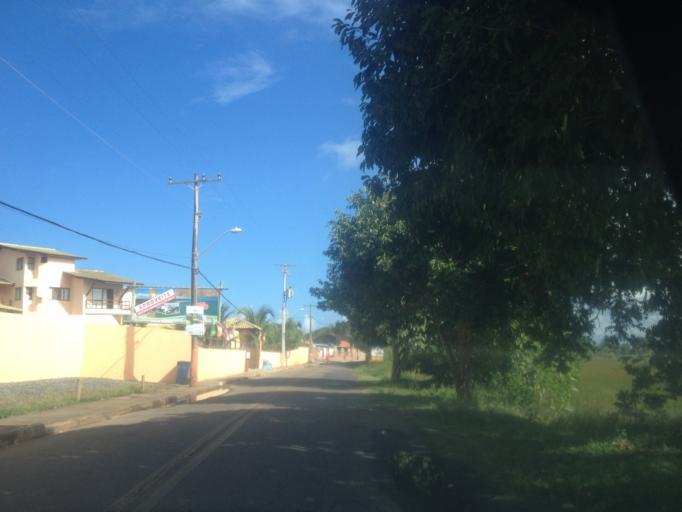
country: BR
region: Bahia
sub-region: Mata De Sao Joao
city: Mata de Sao Joao
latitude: -12.6229
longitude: -38.0477
